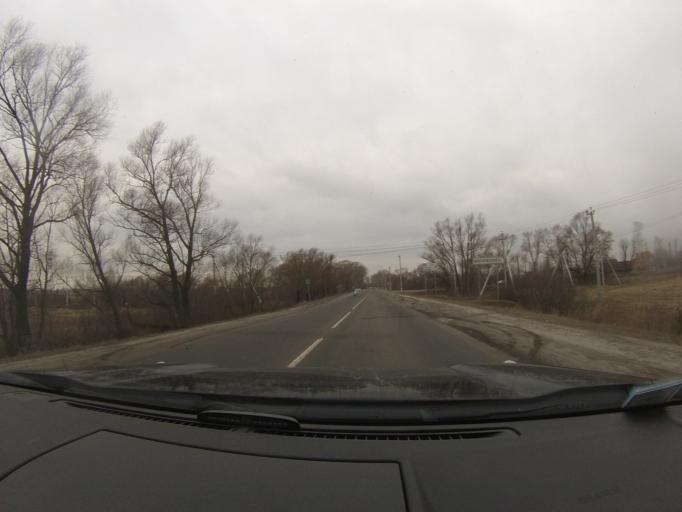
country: RU
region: Moskovskaya
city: Lopatinskiy
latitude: 55.3284
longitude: 38.7233
